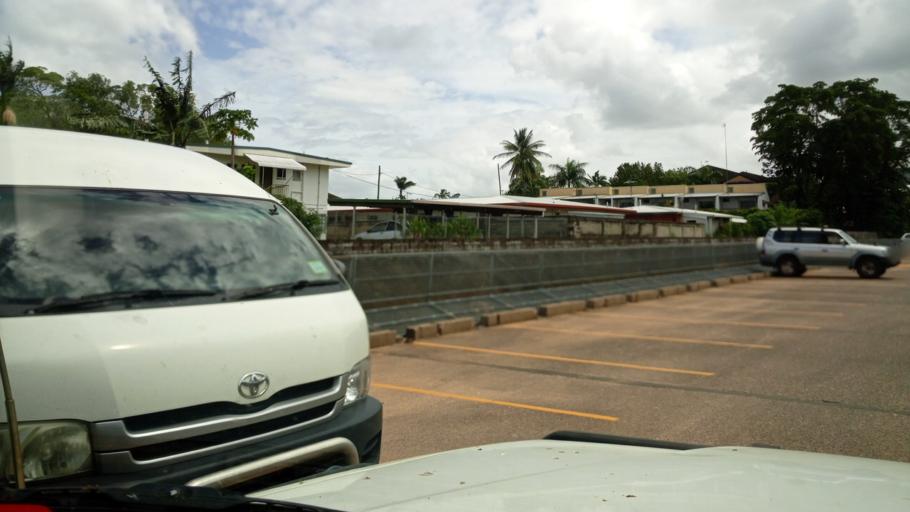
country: AU
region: Queensland
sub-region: Cairns
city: Woree
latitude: -16.9439
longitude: 145.7416
